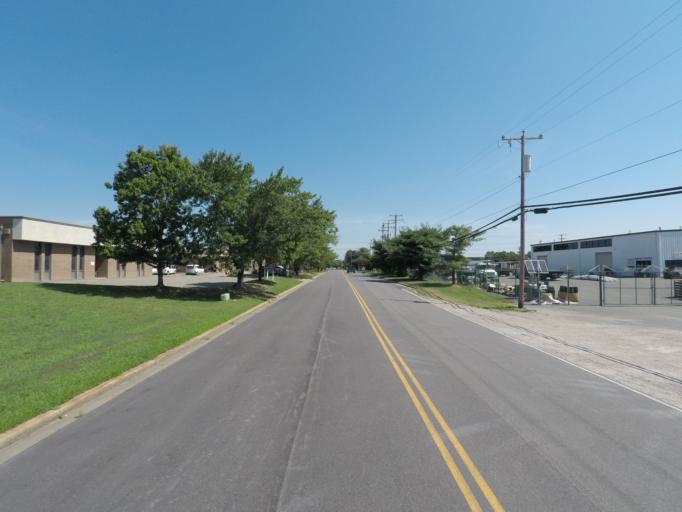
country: US
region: Virginia
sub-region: Henrico County
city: Dumbarton
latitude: 37.5798
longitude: -77.4818
